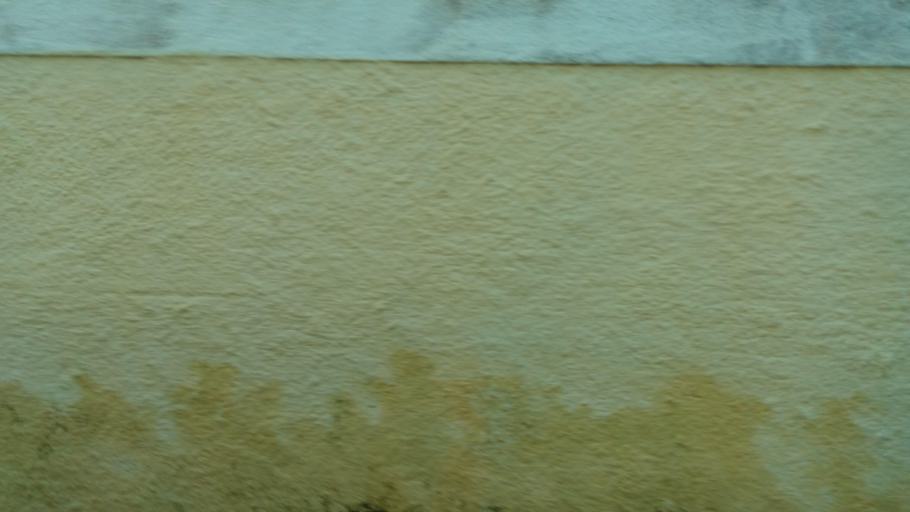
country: BR
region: Pernambuco
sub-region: Palmares
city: Palmares
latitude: -8.6835
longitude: -35.5918
